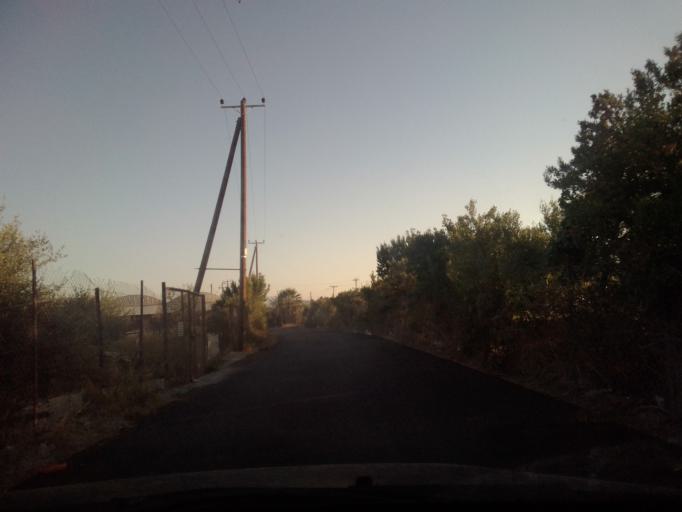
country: CY
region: Limassol
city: Ypsonas
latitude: 34.6707
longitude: 32.9642
